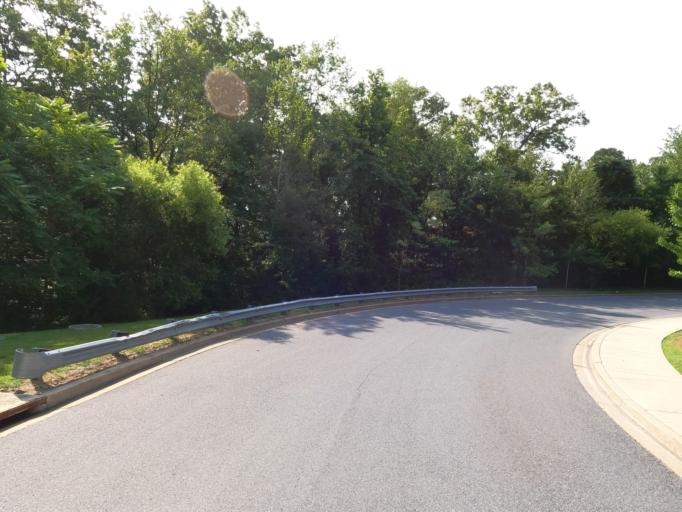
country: US
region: Maryland
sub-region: Anne Arundel County
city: Odenton
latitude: 39.0923
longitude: -76.6990
